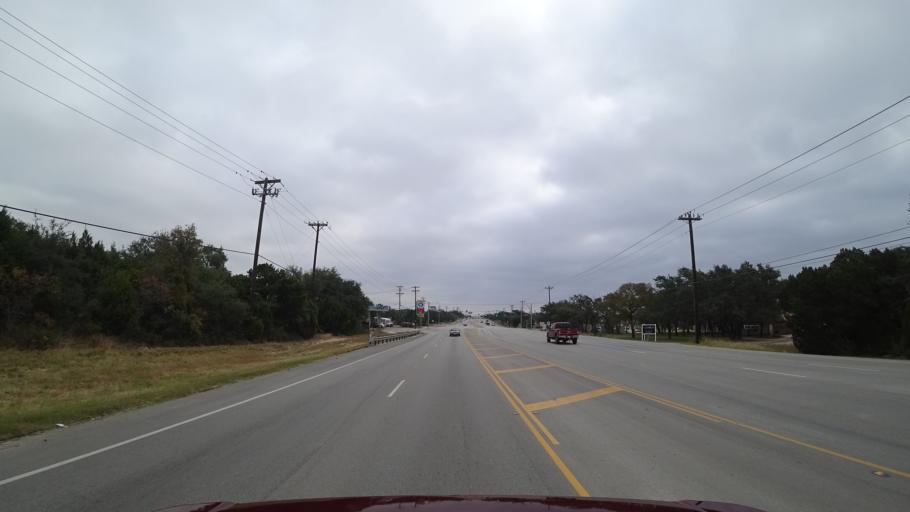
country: US
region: Texas
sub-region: Williamson County
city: Cedar Park
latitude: 30.5173
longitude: -97.8414
